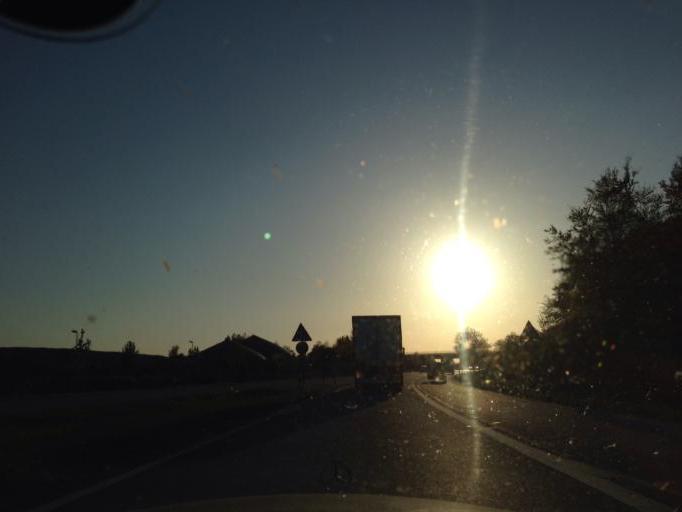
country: DE
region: Schleswig-Holstein
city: Negernbotel
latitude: 53.9696
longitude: 10.2411
